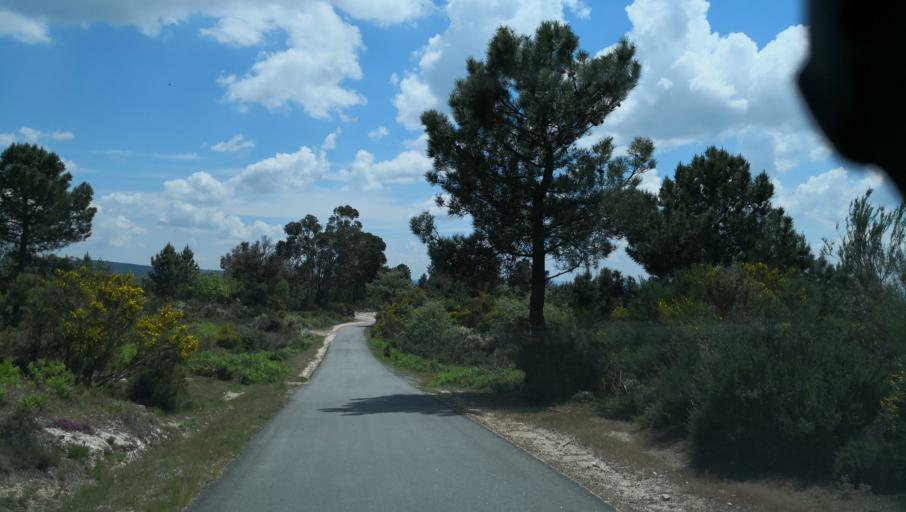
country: PT
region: Vila Real
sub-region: Vila Real
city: Vila Real
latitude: 41.3578
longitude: -7.7375
